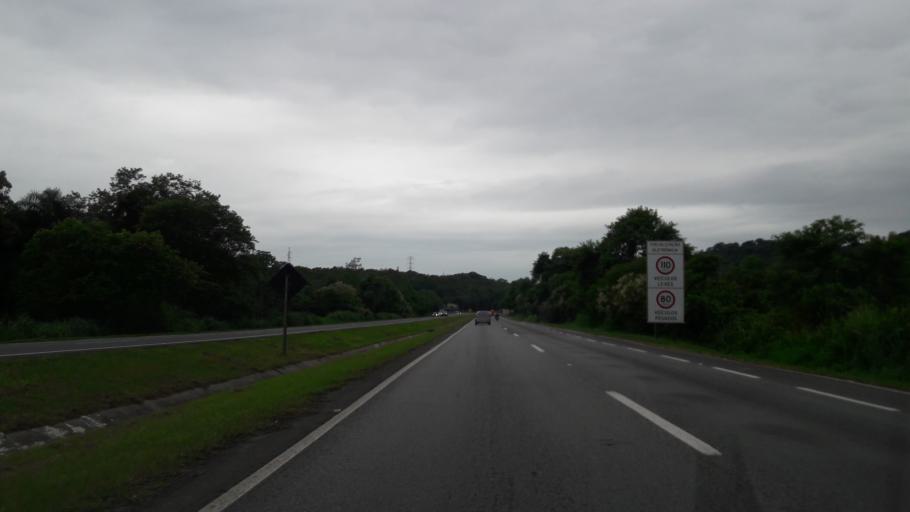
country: BR
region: Parana
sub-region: Antonina
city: Antonina
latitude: -25.5340
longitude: -48.7108
